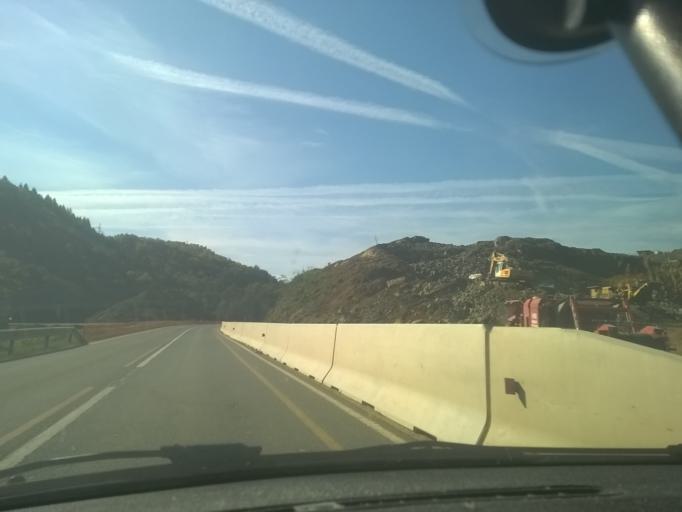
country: SI
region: Podlehnik
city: Podlehnik
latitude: 46.3051
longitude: 15.8607
